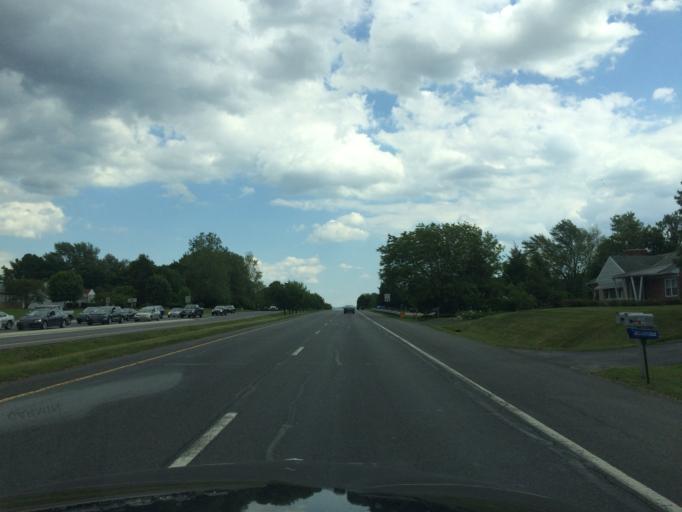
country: US
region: Maryland
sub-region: Washington County
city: Hagerstown
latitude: 39.6238
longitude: -77.6971
